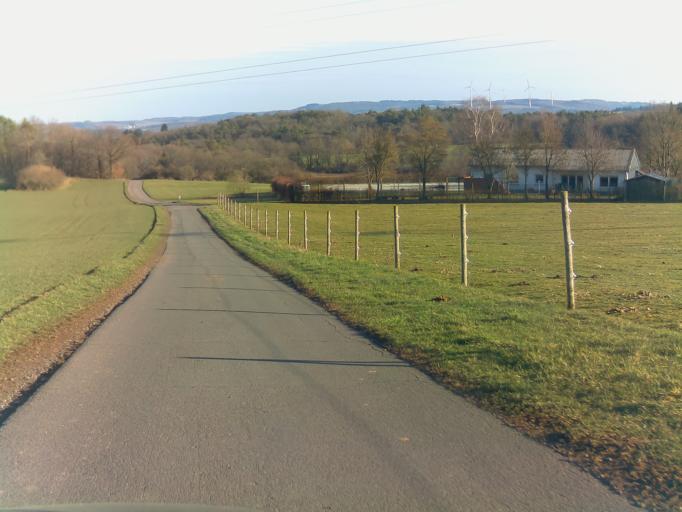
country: DE
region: Rheinland-Pfalz
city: Niederworresbach
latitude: 49.7644
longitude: 7.3573
